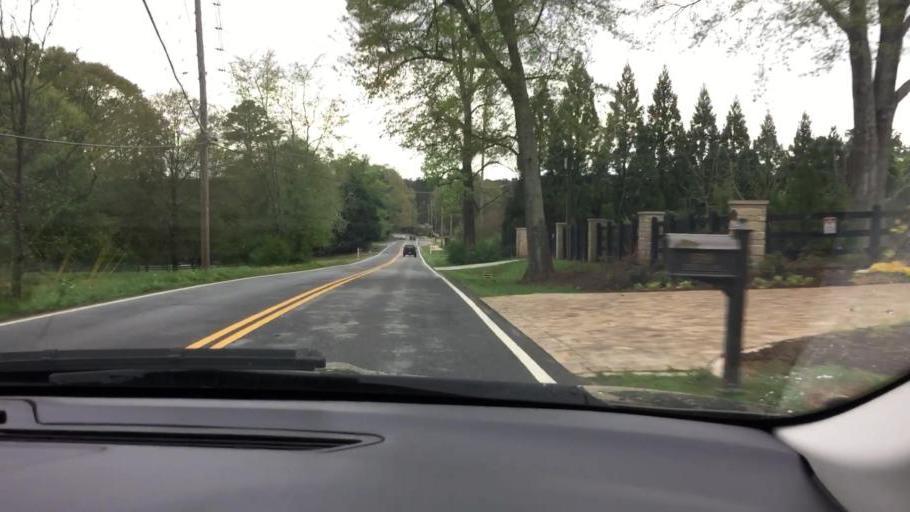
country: US
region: Georgia
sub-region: Fulton County
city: Milton
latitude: 34.1527
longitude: -84.2706
